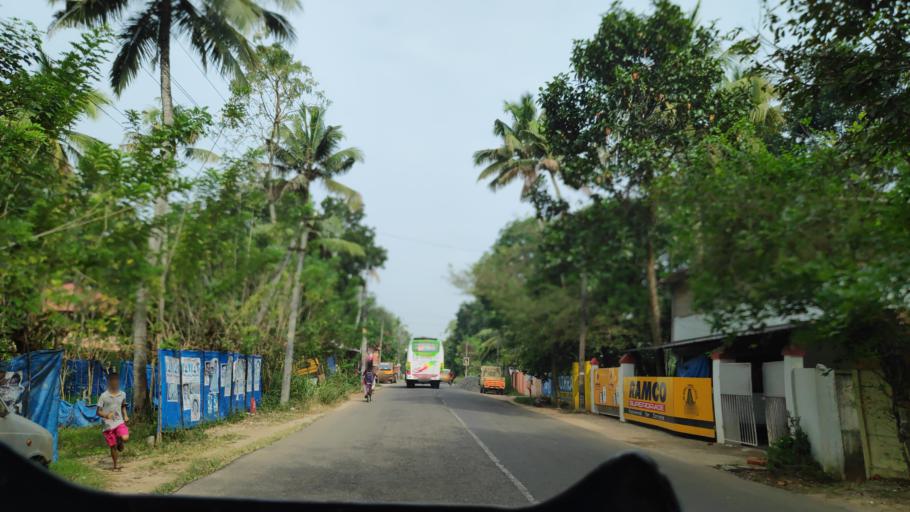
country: IN
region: Kerala
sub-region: Alappuzha
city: Kutiatodu
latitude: 9.8119
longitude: 76.3525
